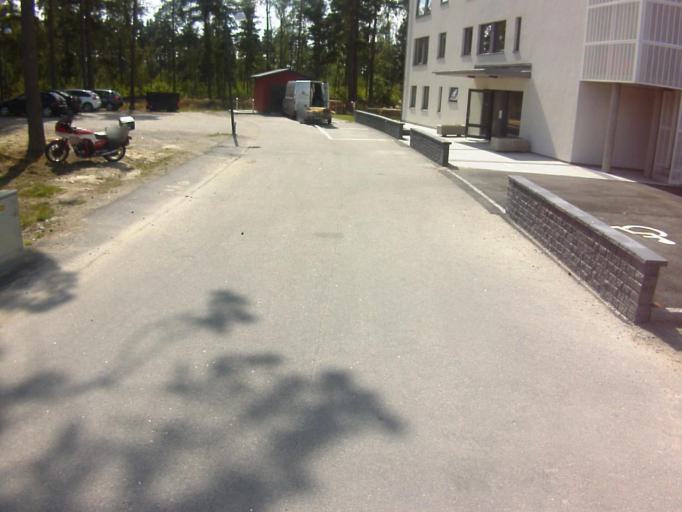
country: SE
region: Blekinge
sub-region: Solvesborgs Kommun
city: Soelvesborg
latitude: 56.0480
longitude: 14.6023
